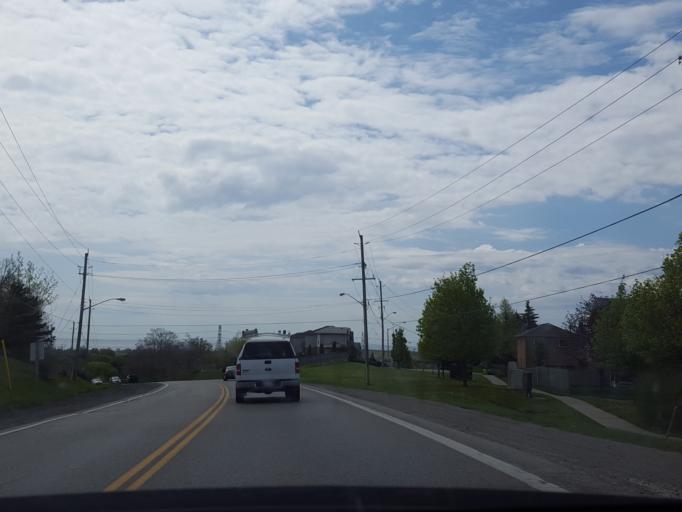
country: CA
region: Ontario
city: Oshawa
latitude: 43.9043
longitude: -78.6991
